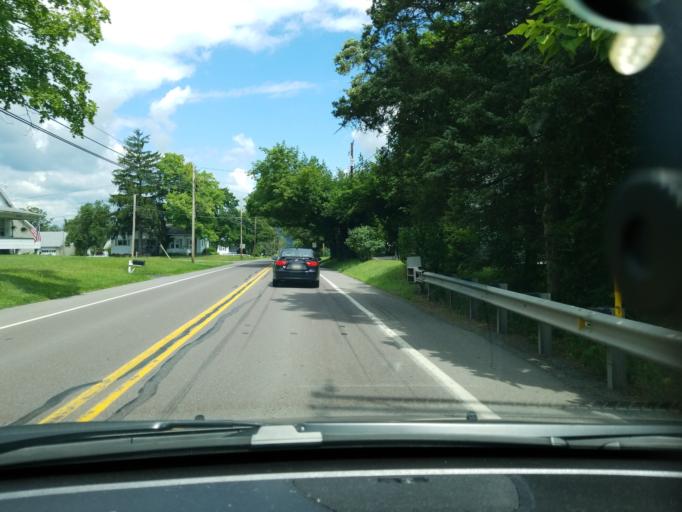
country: US
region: Pennsylvania
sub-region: Northumberland County
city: Elysburg
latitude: 40.8555
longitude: -76.5433
